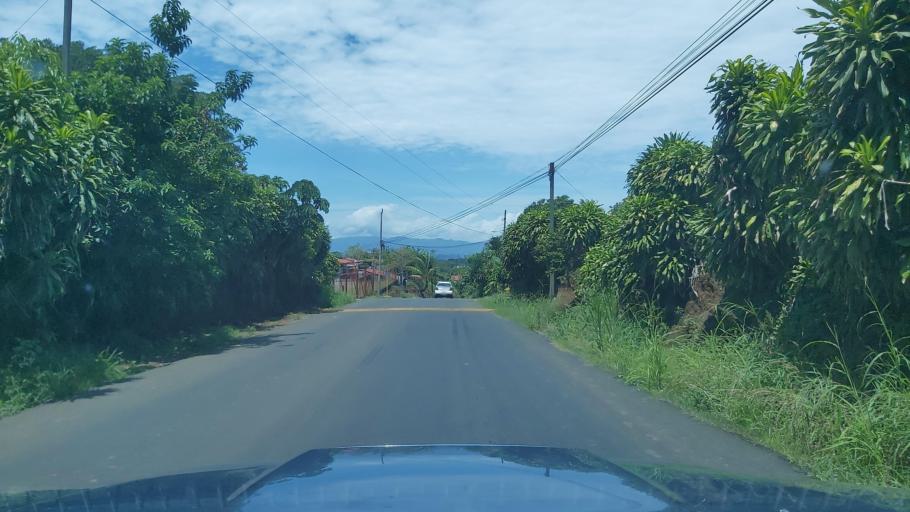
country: CR
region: Alajuela
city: San Juan
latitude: 10.0941
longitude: -84.3399
